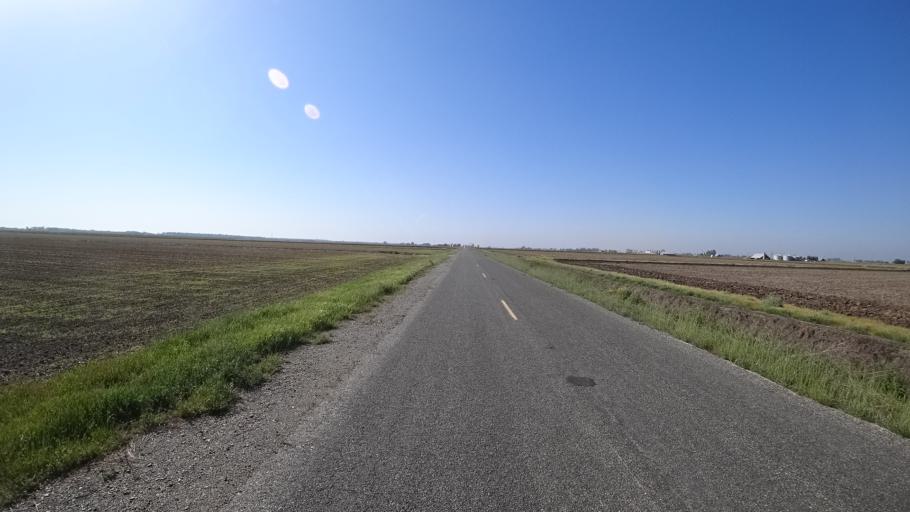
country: US
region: California
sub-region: Glenn County
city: Hamilton City
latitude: 39.6061
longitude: -122.0275
